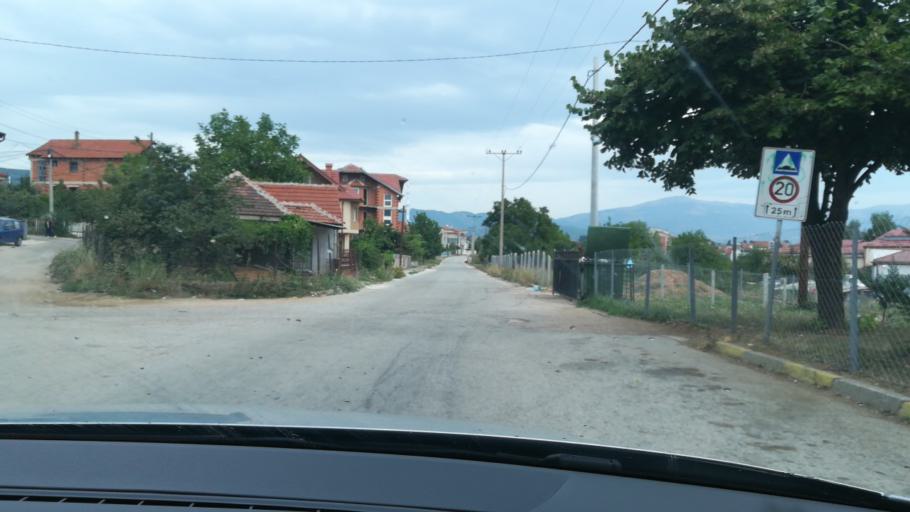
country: MK
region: Kicevo
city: Kicevo
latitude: 41.5160
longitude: 20.9502
